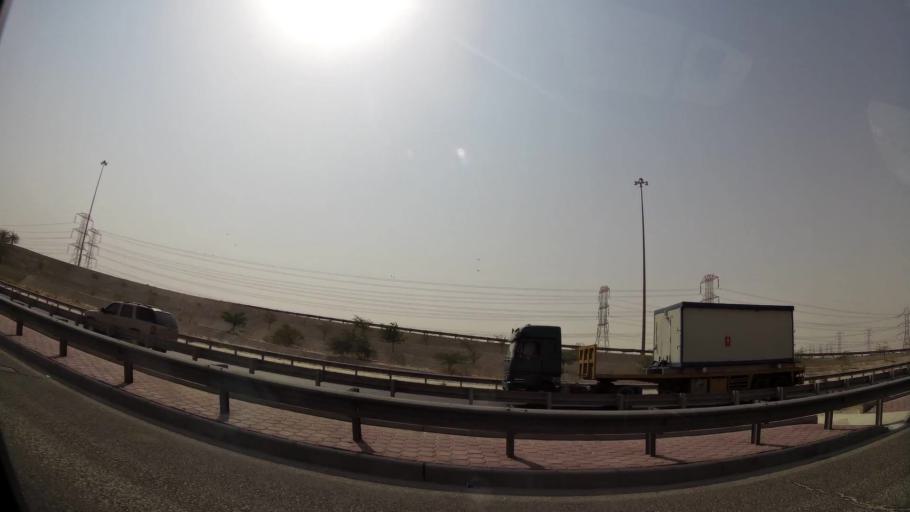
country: KW
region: Muhafazat al Jahra'
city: Al Jahra'
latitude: 29.2988
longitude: 47.7106
